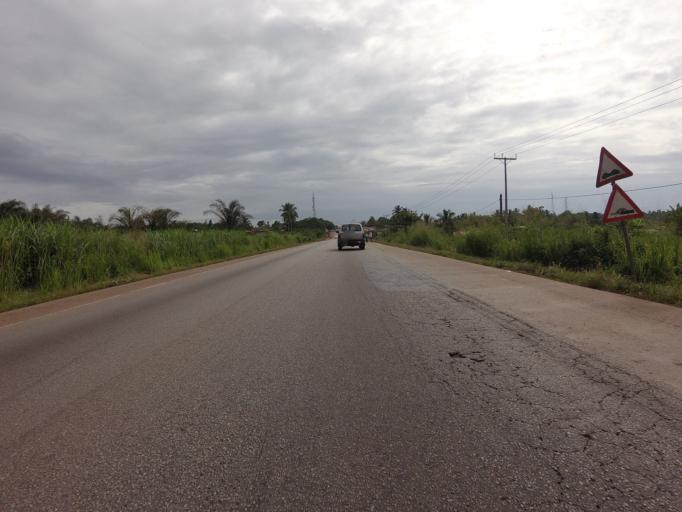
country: GH
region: Eastern
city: Nkawkaw
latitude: 6.5994
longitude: -0.8907
